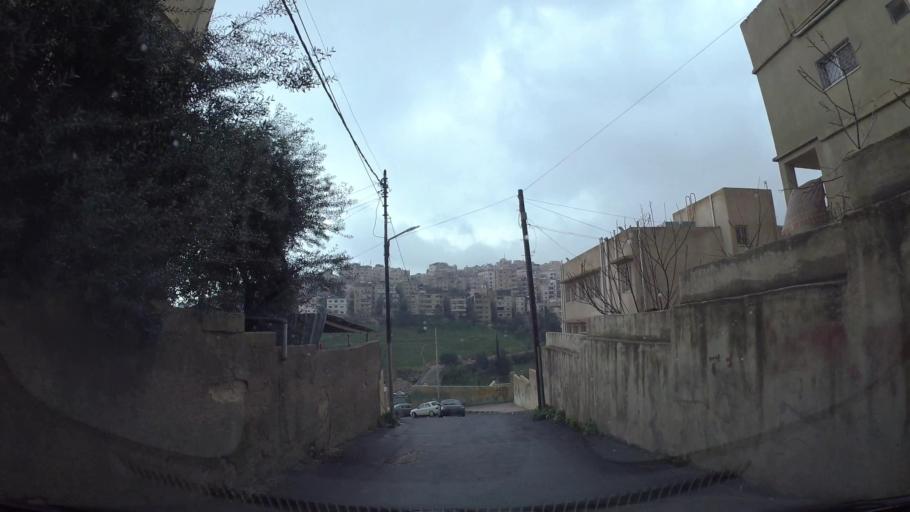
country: JO
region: Amman
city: Amman
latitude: 31.9484
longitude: 35.9107
